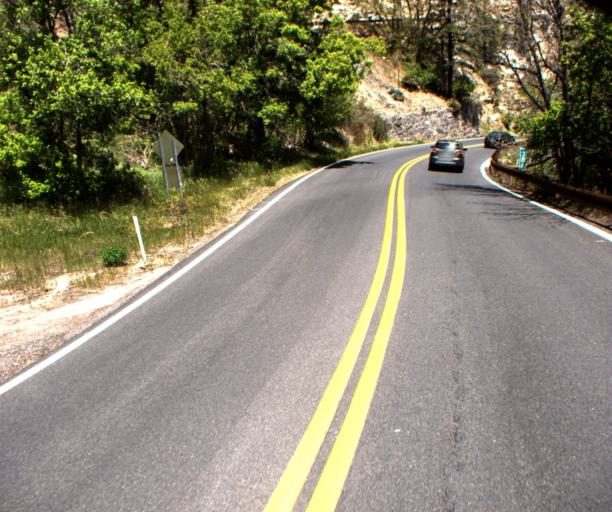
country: US
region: Arizona
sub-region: Coconino County
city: Kachina Village
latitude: 35.0251
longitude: -111.7409
